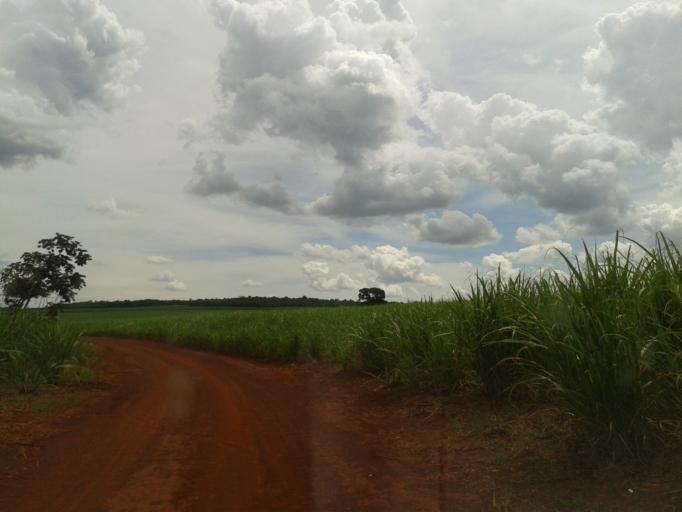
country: BR
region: Minas Gerais
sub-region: Centralina
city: Centralina
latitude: -18.6676
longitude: -49.2407
